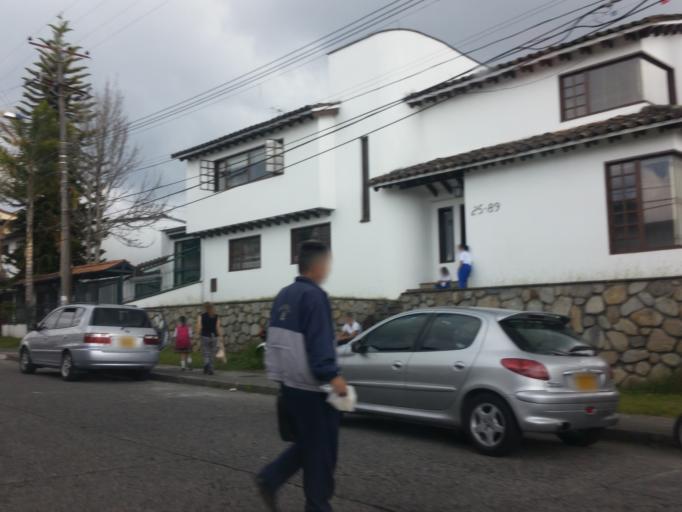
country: CO
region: Caldas
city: Manizales
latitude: 5.0598
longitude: -75.4969
